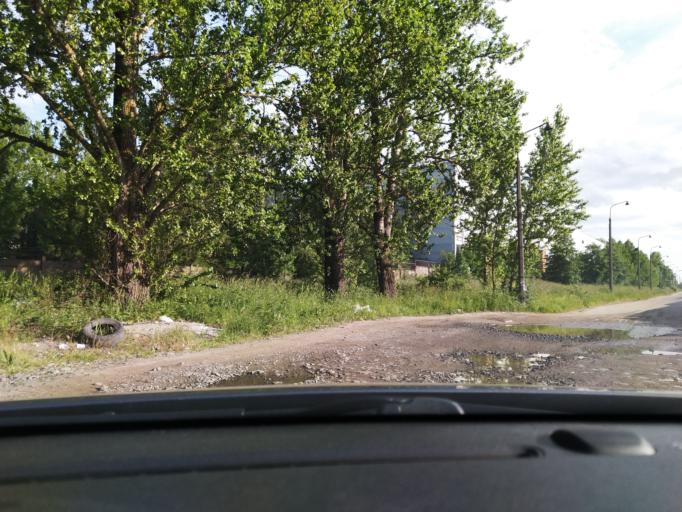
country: RU
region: St.-Petersburg
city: Gorelovo
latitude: 59.7840
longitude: 30.1534
